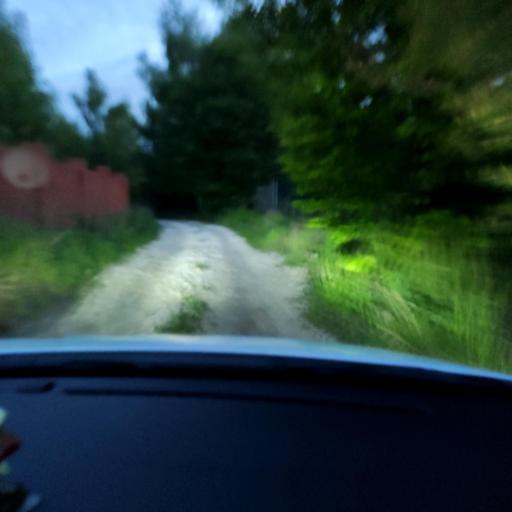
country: RU
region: Tatarstan
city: Stolbishchi
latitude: 55.5932
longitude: 49.0971
